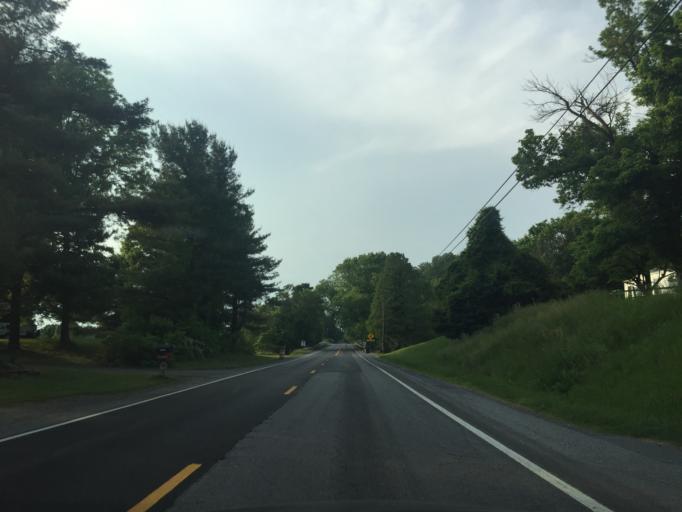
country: US
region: Maryland
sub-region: Frederick County
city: Point of Rocks
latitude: 39.3016
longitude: -77.5420
